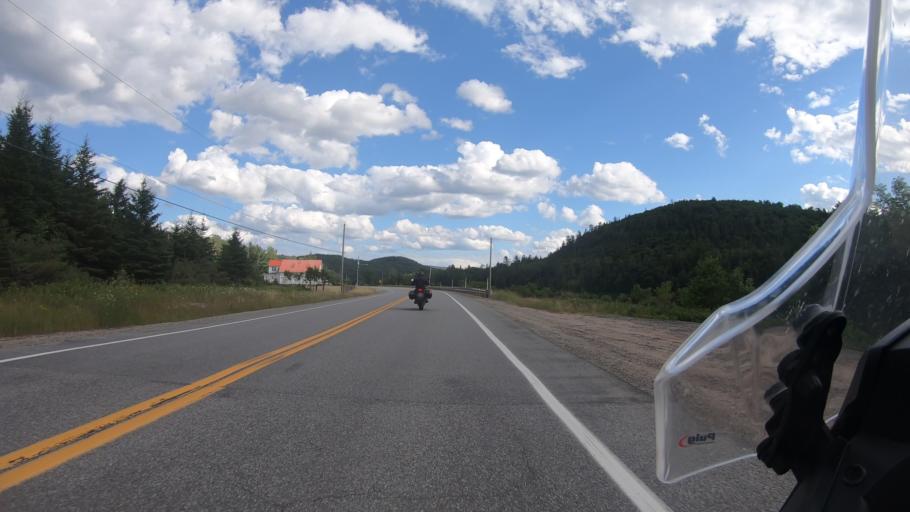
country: CA
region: Quebec
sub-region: Mauricie
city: Saint-Tite
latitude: 46.9870
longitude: -72.9112
